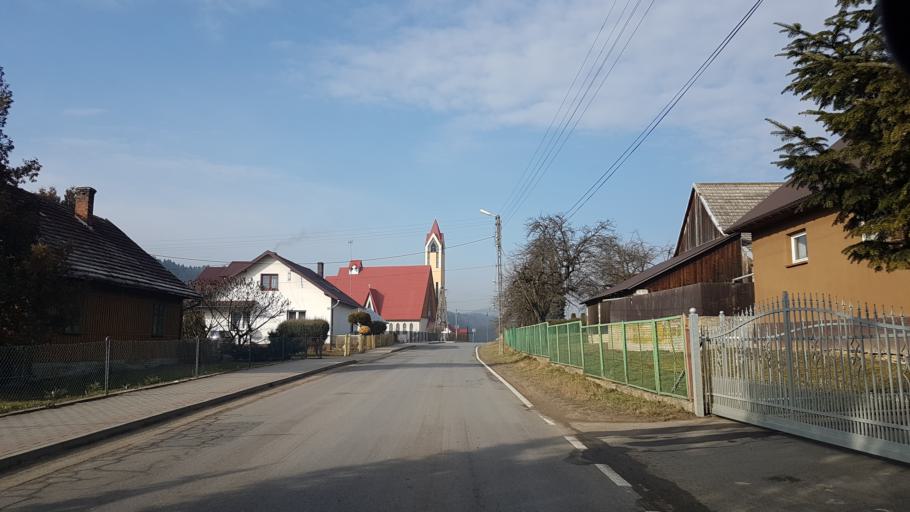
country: PL
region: Lesser Poland Voivodeship
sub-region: Powiat nowosadecki
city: Olszana
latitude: 49.5633
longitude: 20.5553
